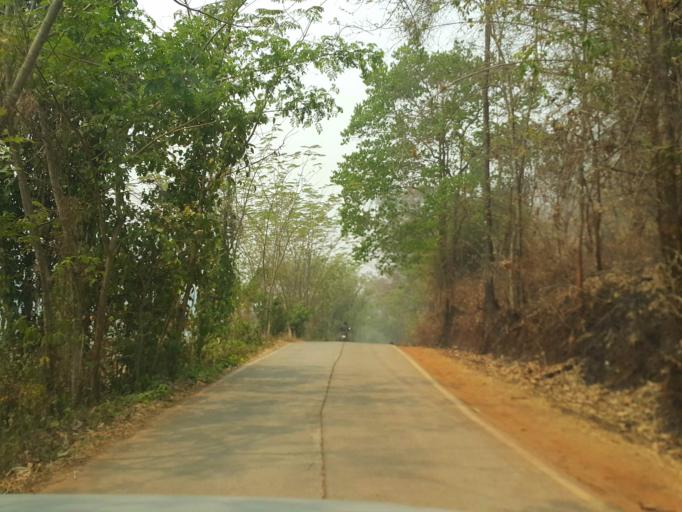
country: TH
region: Chiang Mai
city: Mae Taeng
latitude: 19.2159
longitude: 98.8634
